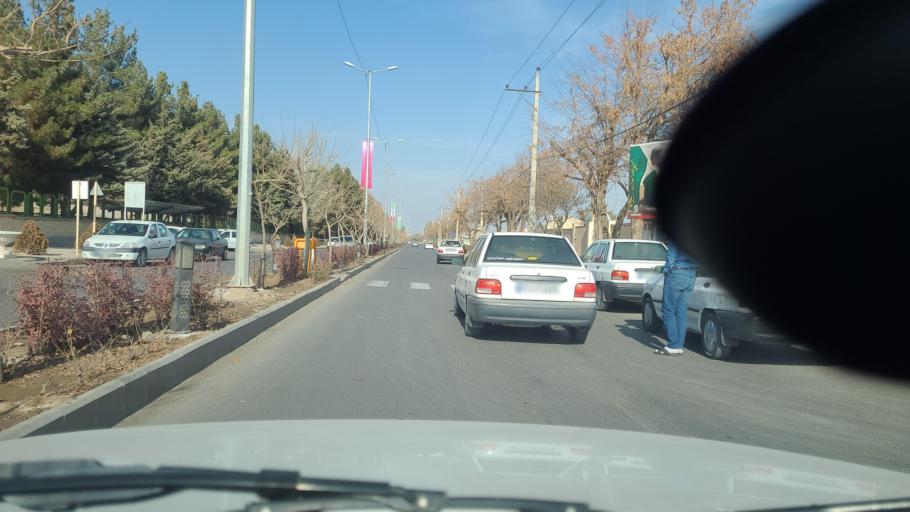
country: IR
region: Razavi Khorasan
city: Fariman
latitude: 35.6896
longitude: 59.8439
